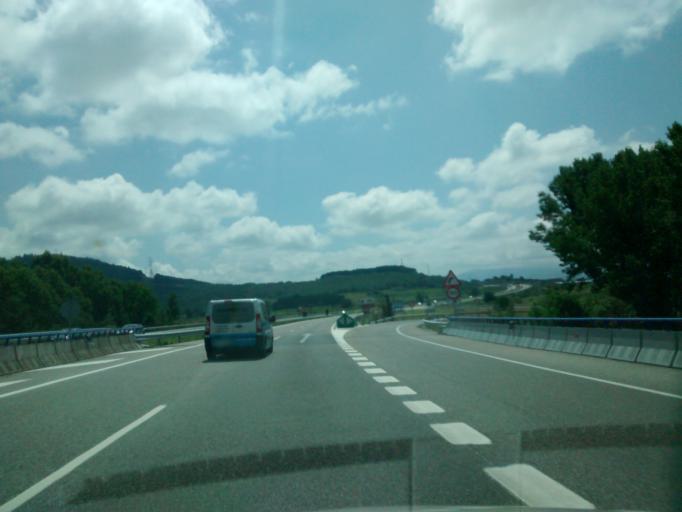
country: ES
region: Castille and Leon
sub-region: Provincia de Leon
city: Ponferrada
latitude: 42.5811
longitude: -6.6069
